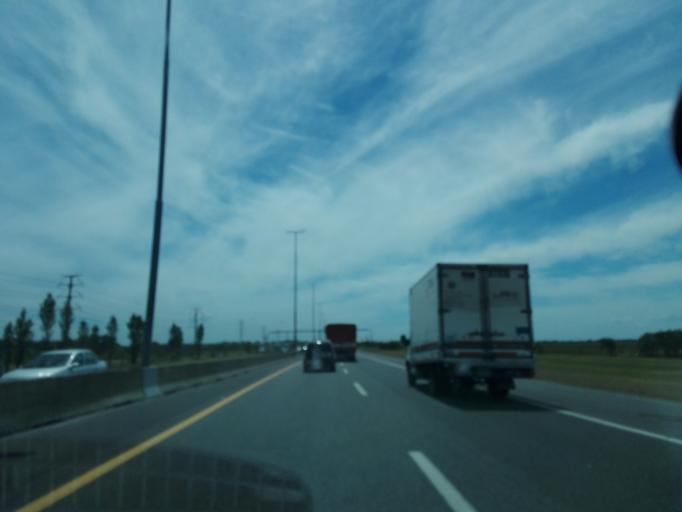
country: AR
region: Buenos Aires
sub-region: Partido de La Plata
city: La Plata
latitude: -34.8334
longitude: -58.0824
